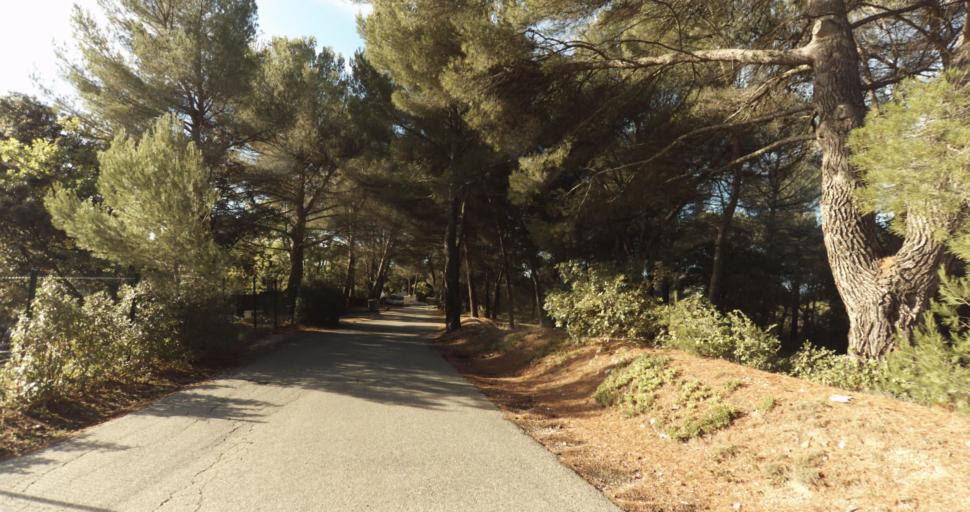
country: FR
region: Provence-Alpes-Cote d'Azur
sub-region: Departement des Bouches-du-Rhone
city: Venelles
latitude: 43.5937
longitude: 5.4694
